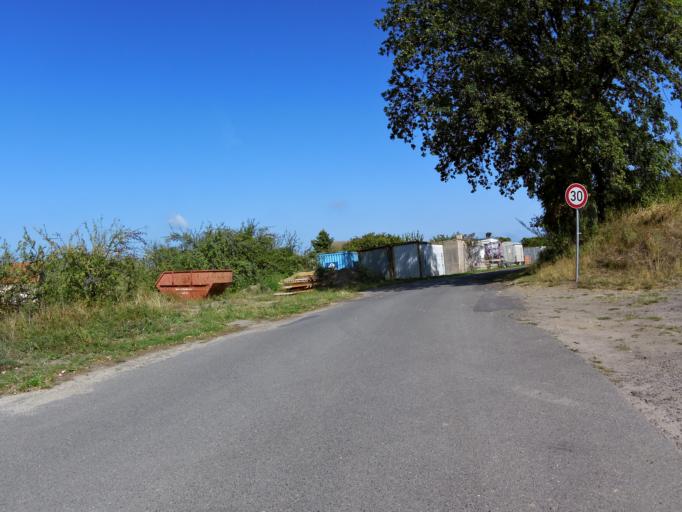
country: DE
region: Mecklenburg-Vorpommern
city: Seebad Bansin
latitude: 53.9663
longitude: 14.0675
